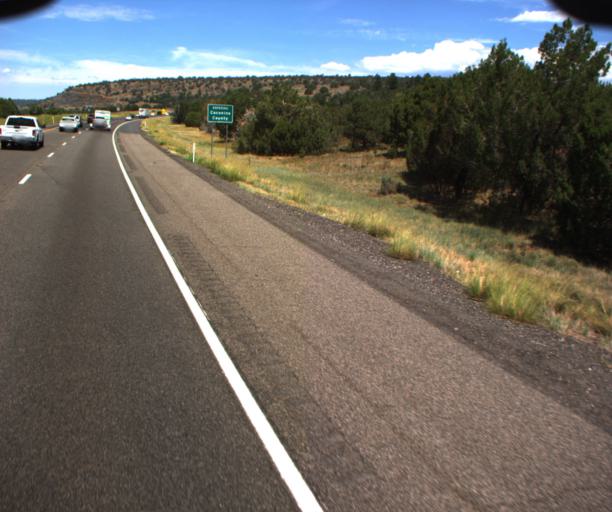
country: US
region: Arizona
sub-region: Yavapai County
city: Village of Oak Creek (Big Park)
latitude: 34.8021
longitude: -111.5955
